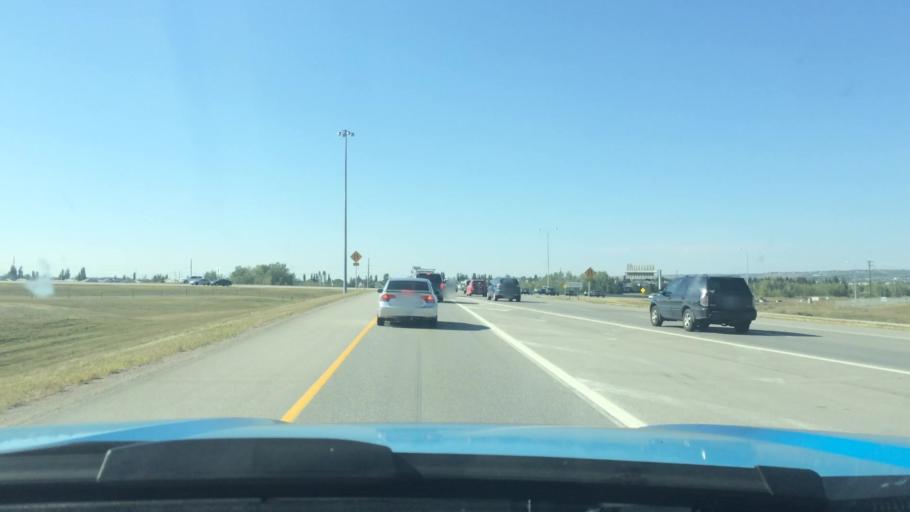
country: CA
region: Alberta
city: Calgary
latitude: 51.0903
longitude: -114.2306
